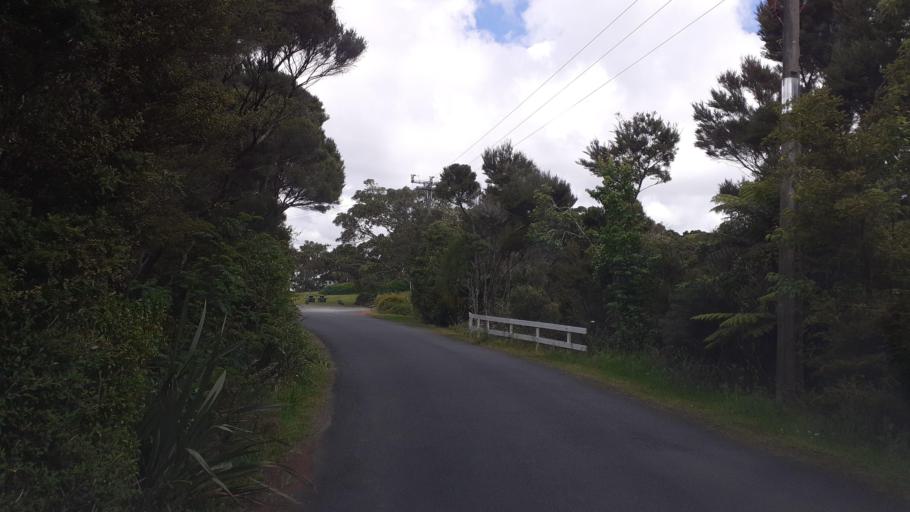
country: NZ
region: Northland
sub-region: Far North District
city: Paihia
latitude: -35.3119
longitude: 174.1132
